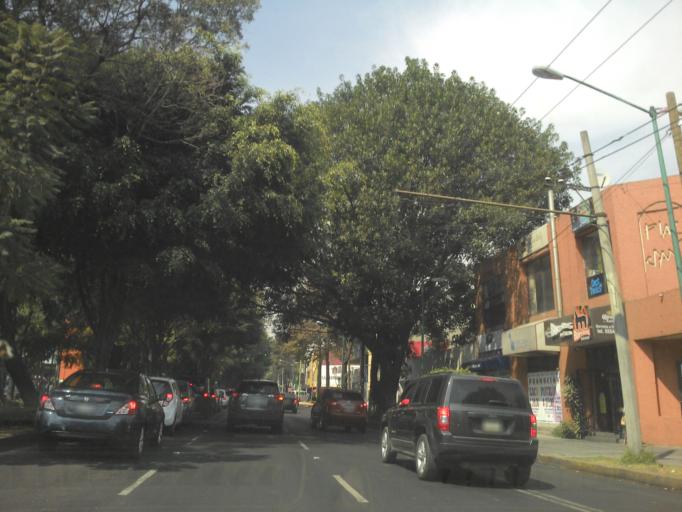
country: MX
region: Mexico City
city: Coyoacan
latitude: 19.3455
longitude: -99.1702
